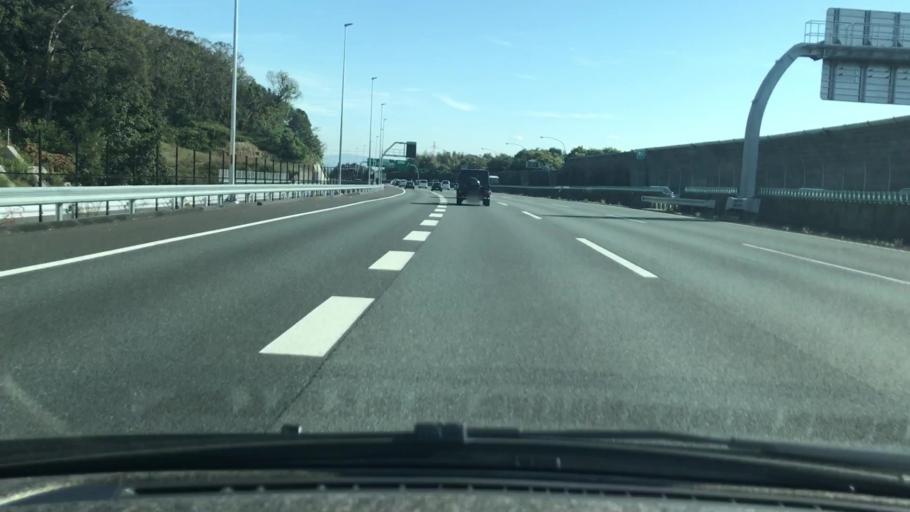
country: JP
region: Osaka
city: Takatsuki
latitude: 34.8633
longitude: 135.6369
